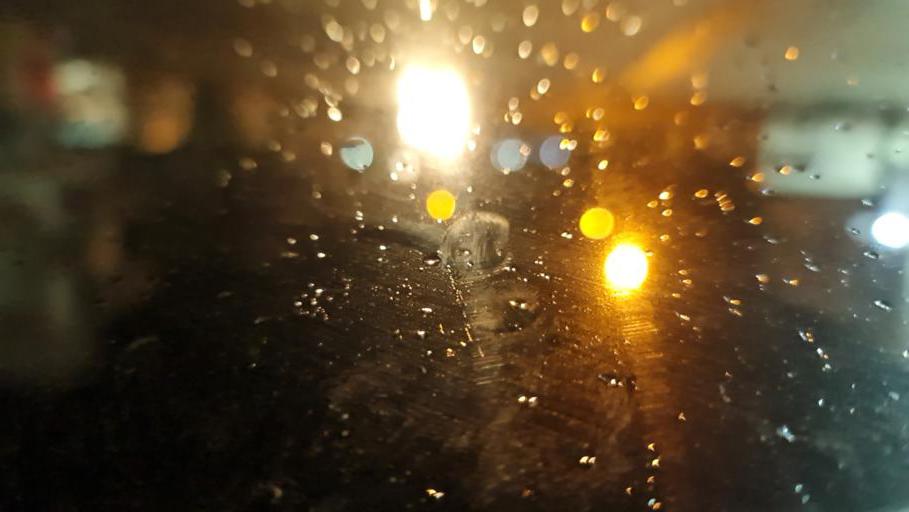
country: MZ
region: Nampula
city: Nampula
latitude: -15.1125
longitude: 39.2853
